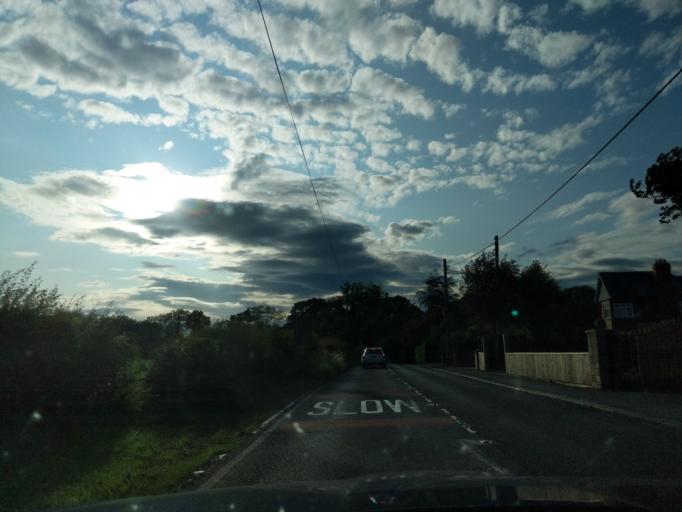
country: GB
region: England
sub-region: Northumberland
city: Bedlington
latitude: 55.1233
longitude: -1.5798
